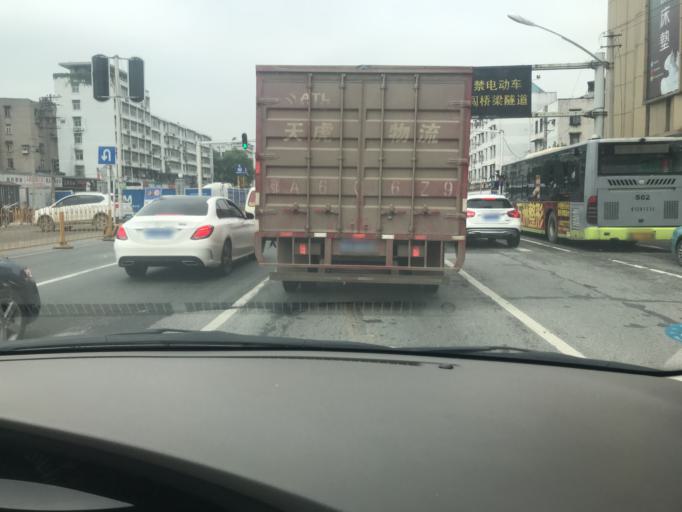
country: CN
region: Hubei
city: Jiang'an
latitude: 30.6117
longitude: 114.3483
